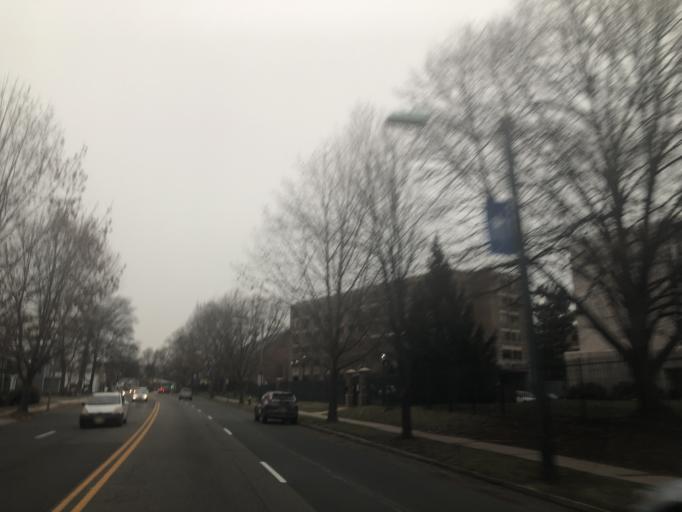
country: US
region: New Jersey
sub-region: Essex County
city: South Orange
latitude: 40.7448
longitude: -74.2455
